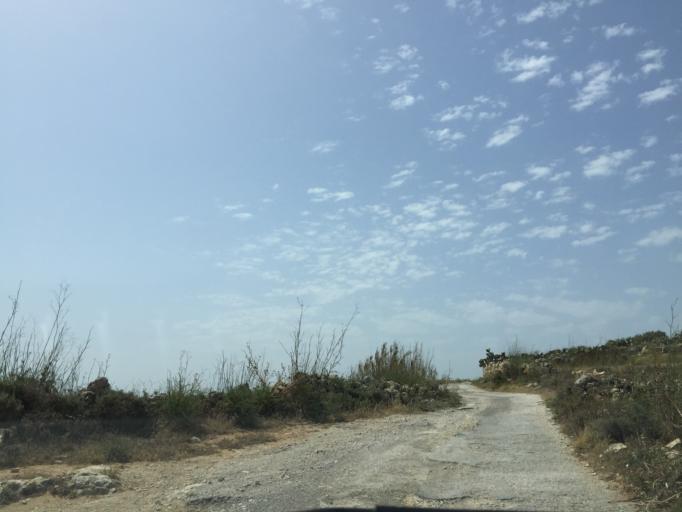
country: MT
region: In-Nadur
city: Nadur
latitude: 36.0607
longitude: 14.2906
